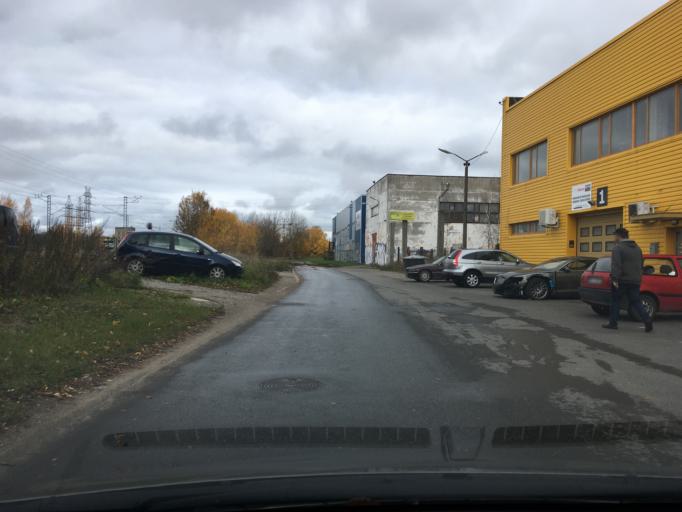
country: EE
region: Harju
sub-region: Tallinna linn
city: Tallinn
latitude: 59.3953
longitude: 24.7206
